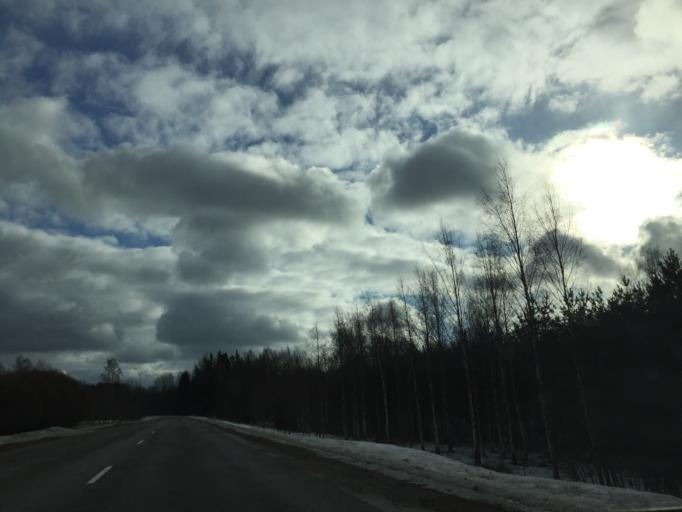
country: LV
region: Aloja
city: Staicele
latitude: 57.8522
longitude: 24.7099
